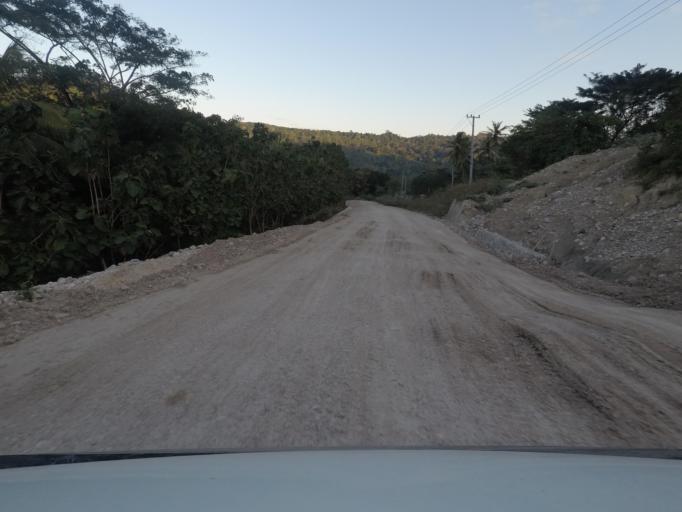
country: TL
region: Lautem
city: Lospalos
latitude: -8.3957
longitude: 127.2552
